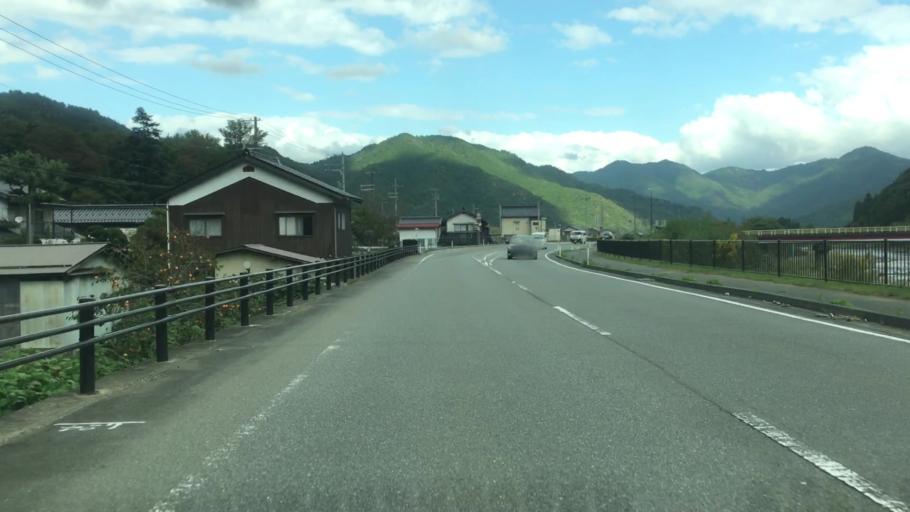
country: JP
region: Hyogo
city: Toyooka
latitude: 35.3708
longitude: 134.7633
